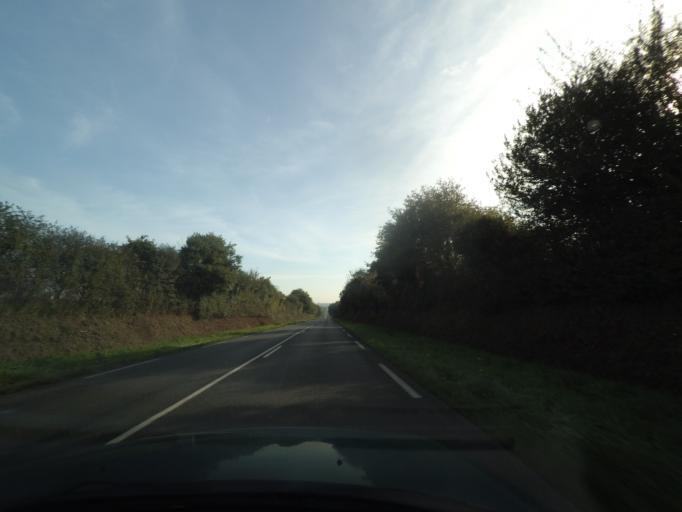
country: FR
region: Pays de la Loire
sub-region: Departement de Maine-et-Loire
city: La Seguiniere
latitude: 47.0574
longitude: -0.9659
